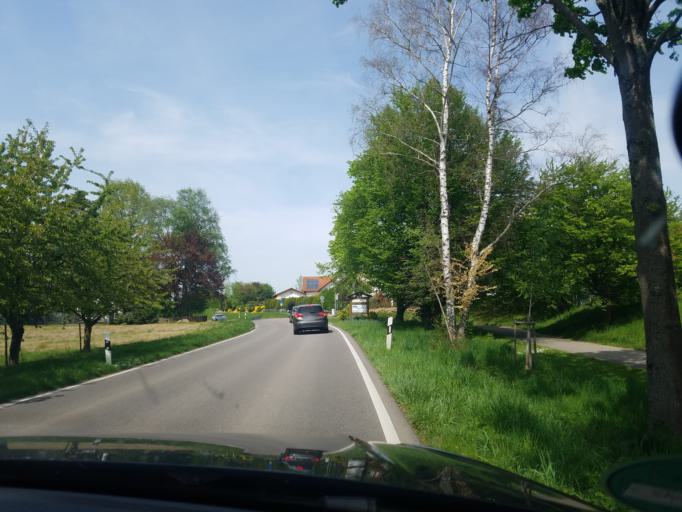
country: DE
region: Baden-Wuerttemberg
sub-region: Freiburg Region
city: Haslach
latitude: 48.5618
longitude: 8.0600
